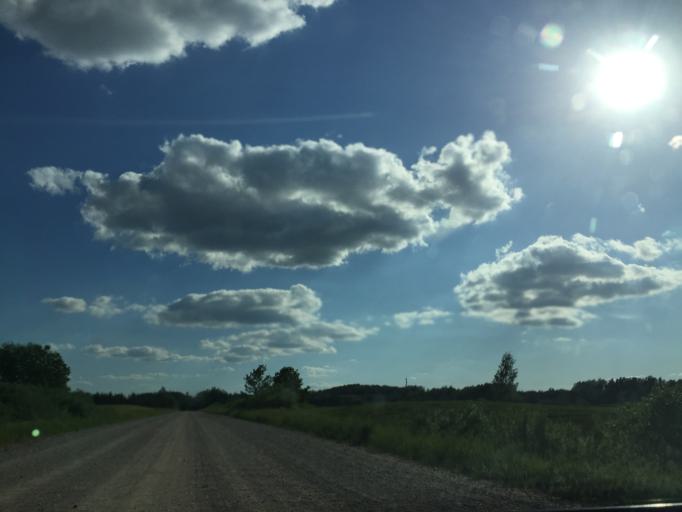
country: LV
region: Kandava
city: Kandava
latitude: 56.8875
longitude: 22.7815
